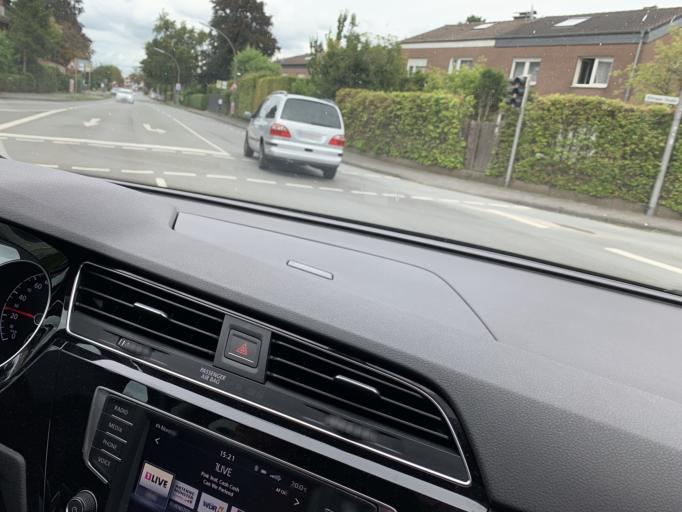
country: DE
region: North Rhine-Westphalia
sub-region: Regierungsbezirk Munster
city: Telgte
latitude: 51.9120
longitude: 7.7222
